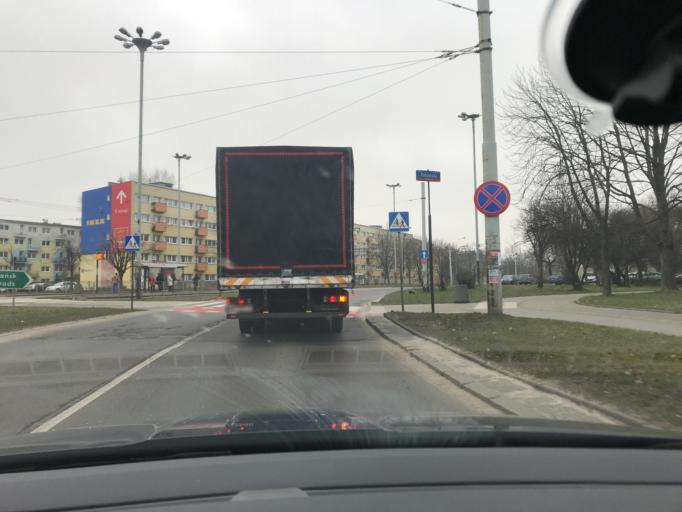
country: PL
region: Lodz Voivodeship
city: Lodz
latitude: 51.7313
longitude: 19.4522
